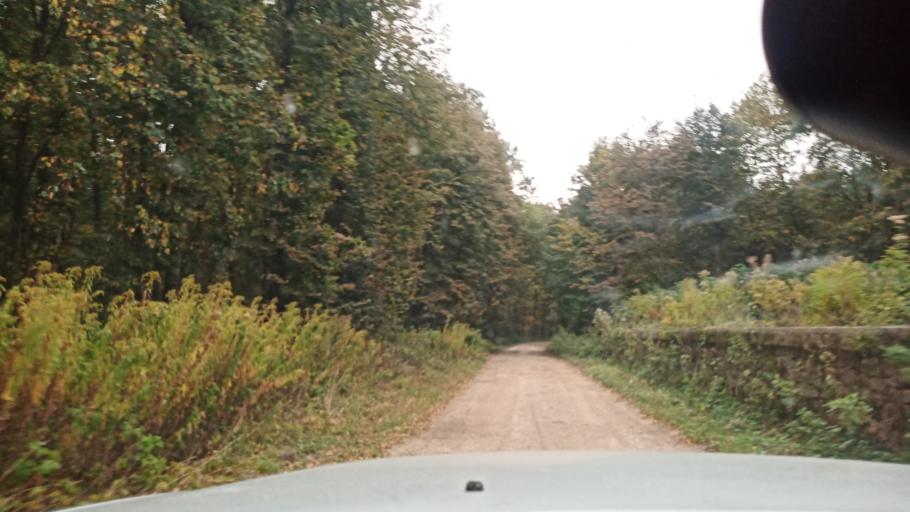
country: HU
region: Fejer
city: Mor
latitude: 47.3838
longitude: 18.2536
